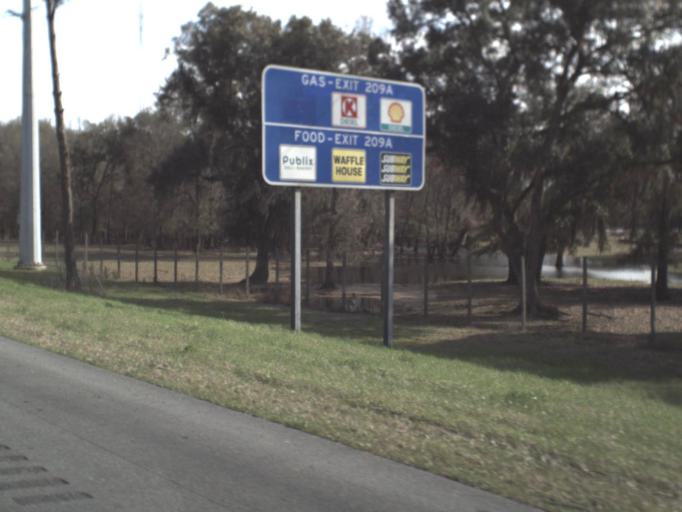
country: US
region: Florida
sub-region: Leon County
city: Tallahassee
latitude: 30.4894
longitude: -84.1650
